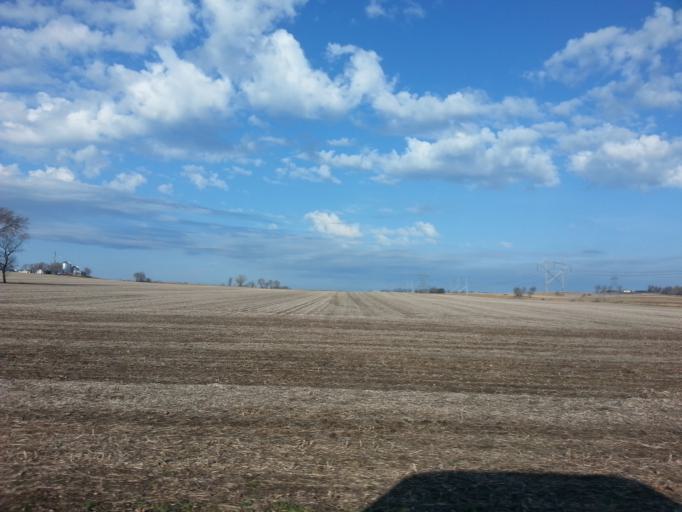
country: US
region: Minnesota
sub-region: Washington County
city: Afton
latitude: 44.8542
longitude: -92.8422
